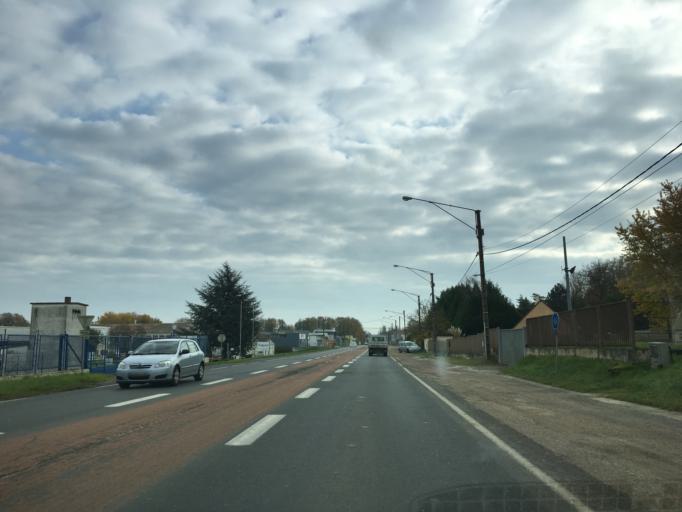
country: FR
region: Bourgogne
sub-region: Departement de l'Yonne
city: Pont-sur-Yonne
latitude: 48.2930
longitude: 3.1967
